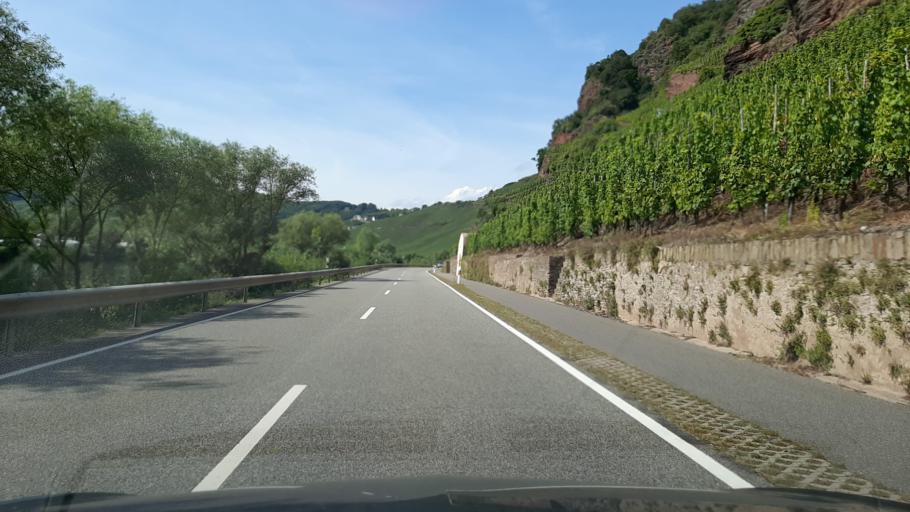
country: DE
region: Rheinland-Pfalz
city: Erden
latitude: 49.9815
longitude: 7.0256
